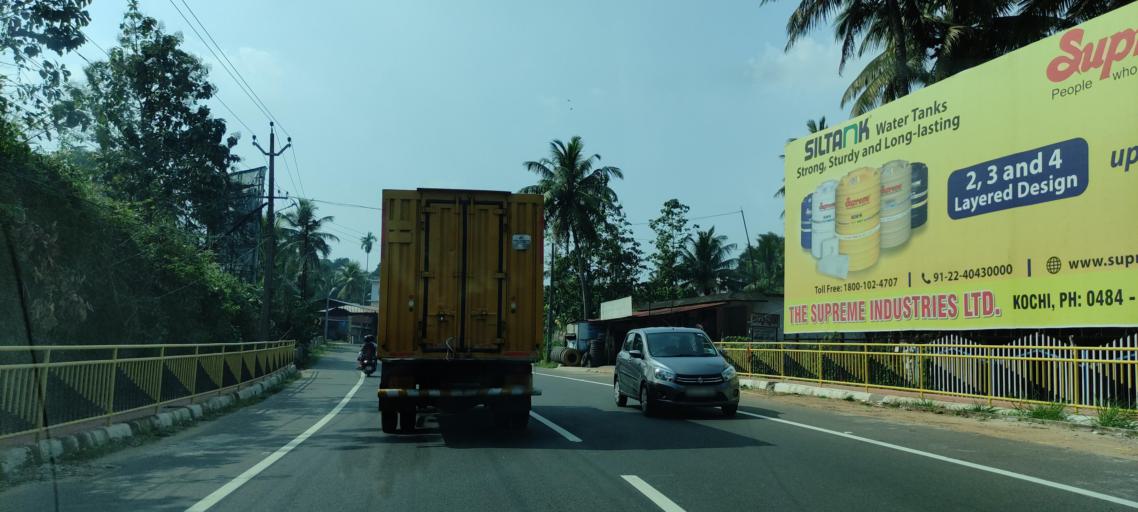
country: IN
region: Kerala
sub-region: Alappuzha
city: Chengannur
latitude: 9.2926
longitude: 76.6456
